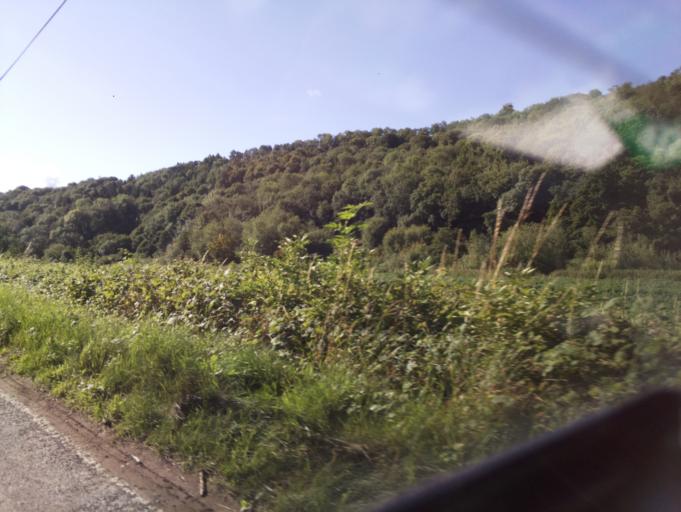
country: GB
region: England
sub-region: Herefordshire
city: Walford
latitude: 51.8652
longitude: -2.6045
